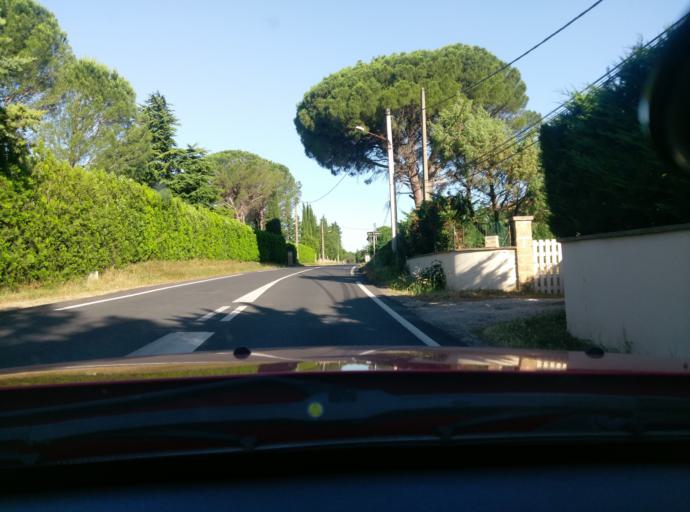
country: FR
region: Languedoc-Roussillon
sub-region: Departement du Gard
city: Castillon-du-Gard
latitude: 43.9529
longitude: 4.5518
